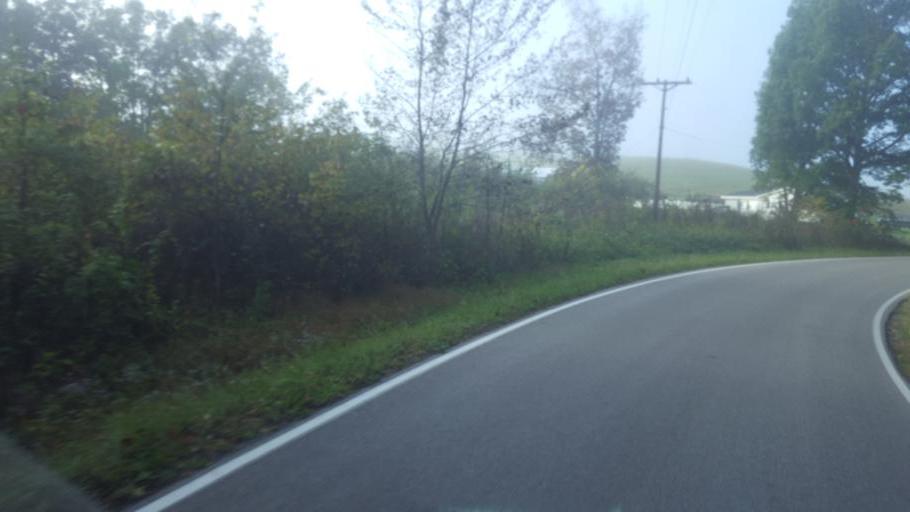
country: US
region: Kentucky
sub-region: Fleming County
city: Flemingsburg
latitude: 38.4987
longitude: -83.5560
